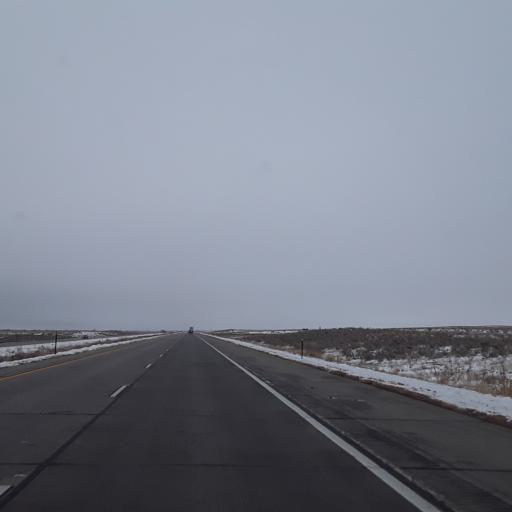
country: US
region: Colorado
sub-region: Logan County
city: Sterling
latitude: 40.5532
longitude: -103.2159
